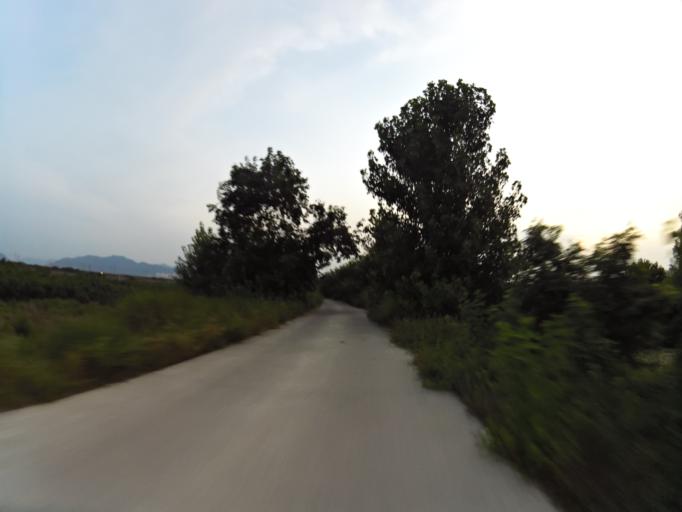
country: KR
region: Gyeongsangbuk-do
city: Gyeongsan-si
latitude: 35.8565
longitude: 128.7469
